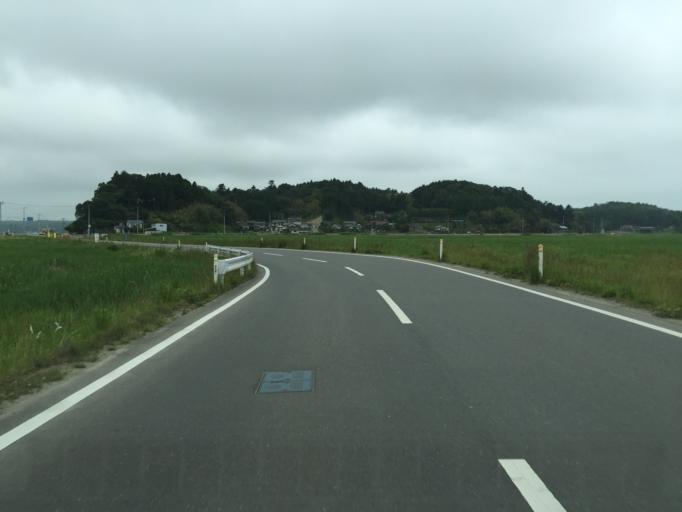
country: JP
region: Fukushima
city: Namie
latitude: 37.7256
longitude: 141.0064
